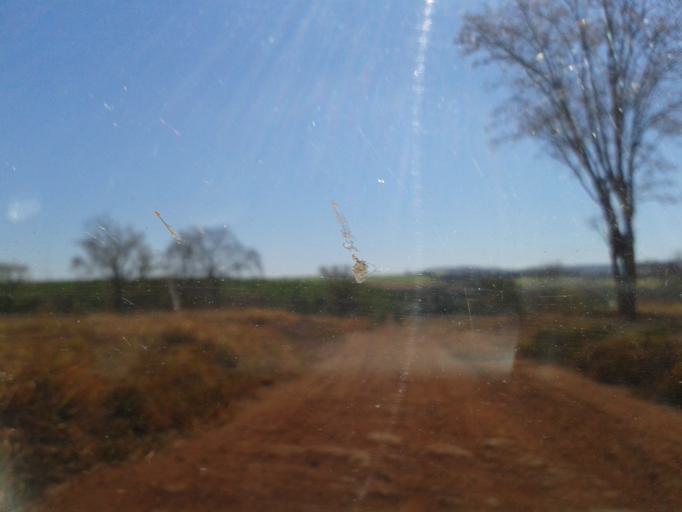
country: BR
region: Minas Gerais
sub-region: Centralina
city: Centralina
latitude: -18.5709
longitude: -49.1353
